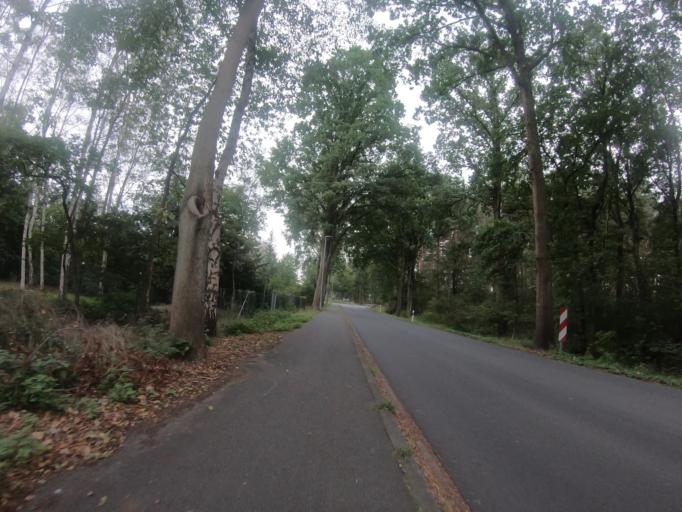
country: DE
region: Lower Saxony
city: Ribbesbuttel
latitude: 52.4515
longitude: 10.4990
